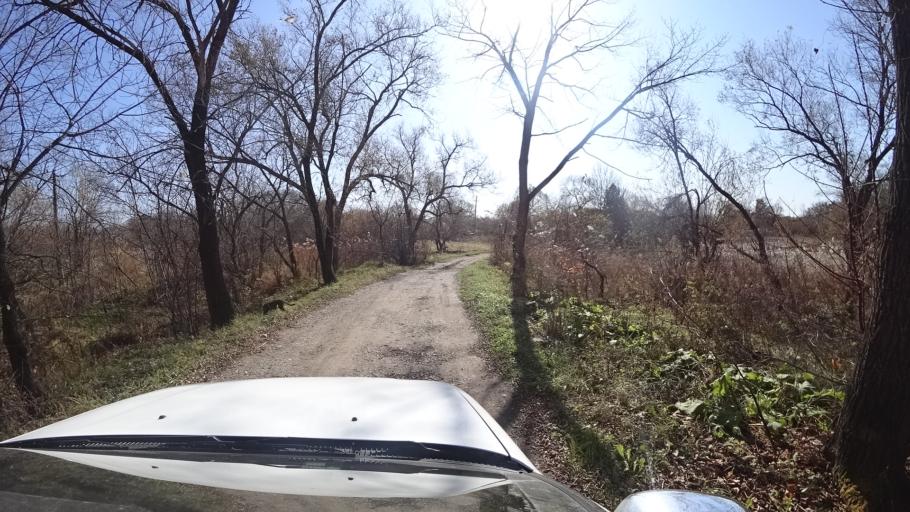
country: RU
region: Primorskiy
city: Dal'nerechensk
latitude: 45.9109
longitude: 133.7960
